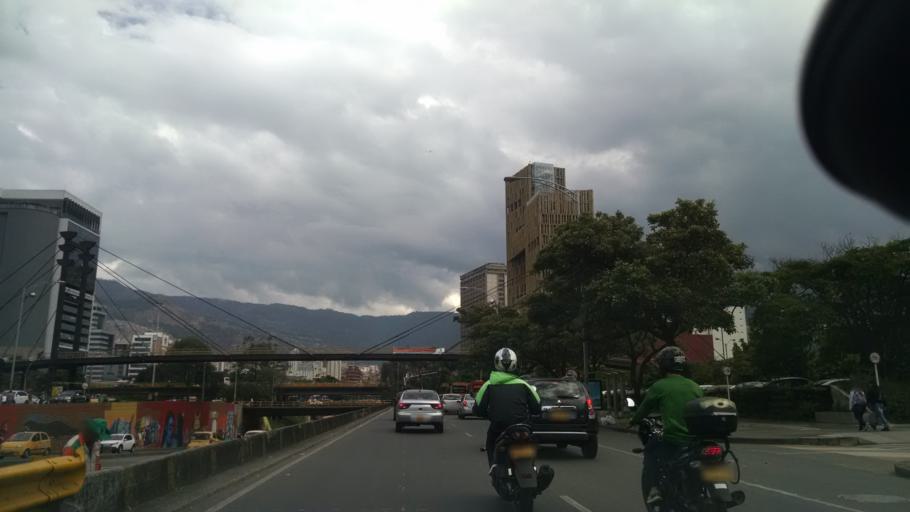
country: CO
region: Antioquia
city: Medellin
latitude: 6.2467
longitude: -75.5770
